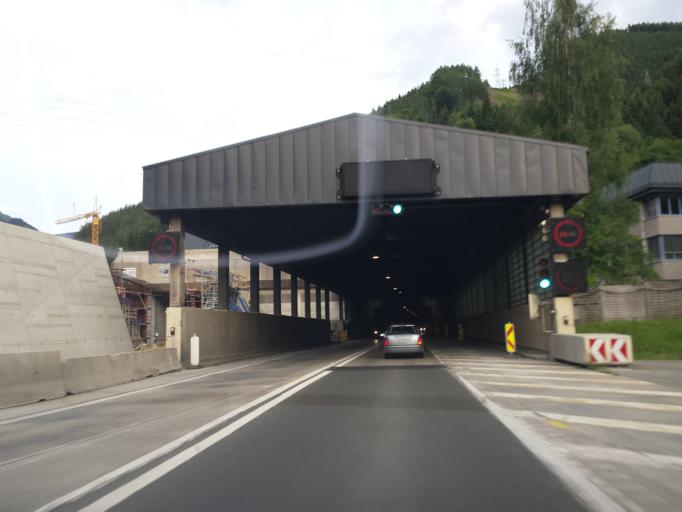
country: AT
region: Styria
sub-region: Politischer Bezirk Leoben
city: Leoben
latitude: 47.2950
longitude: 15.0772
